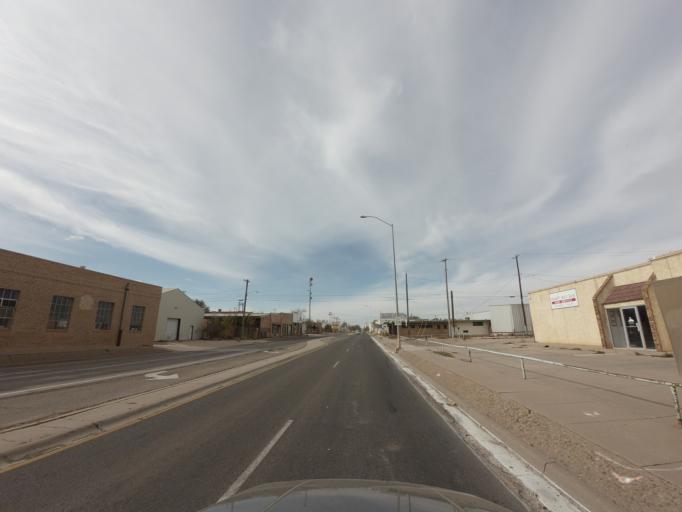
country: US
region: New Mexico
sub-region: Curry County
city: Clovis
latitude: 34.3987
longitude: -103.2055
